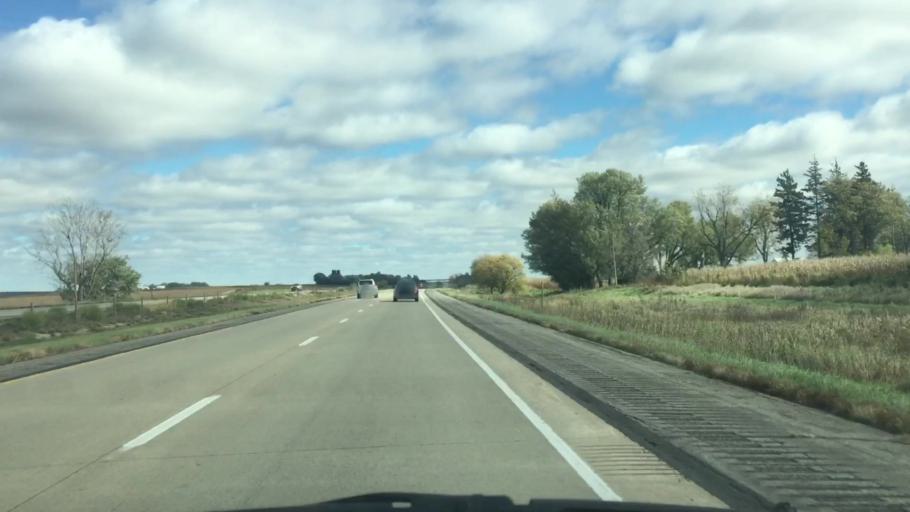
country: US
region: Iowa
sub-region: Poweshiek County
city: Brooklyn
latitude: 41.6962
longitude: -92.2621
